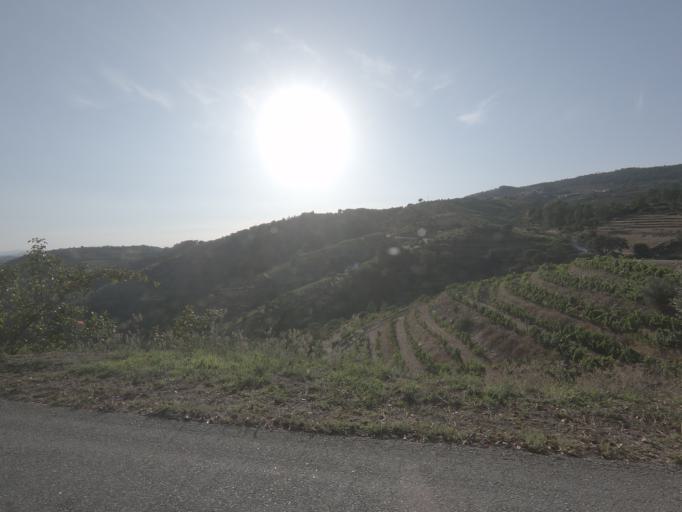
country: PT
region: Vila Real
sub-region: Sabrosa
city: Vilela
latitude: 41.1766
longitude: -7.5972
